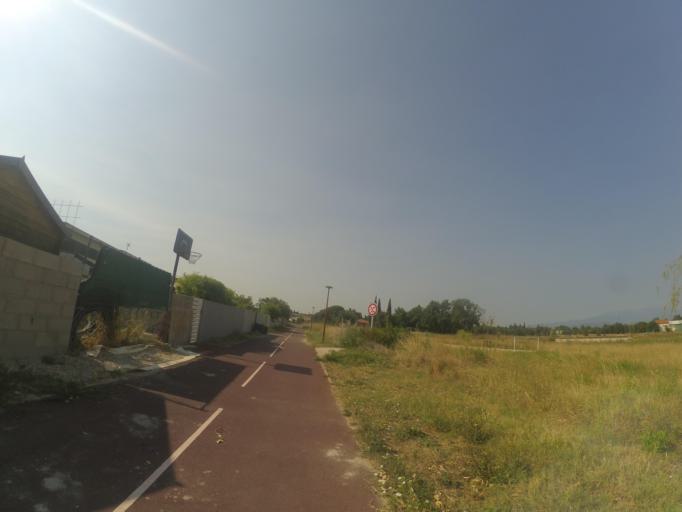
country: FR
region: Languedoc-Roussillon
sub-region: Departement des Pyrenees-Orientales
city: Toulouges
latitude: 42.6665
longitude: 2.8226
